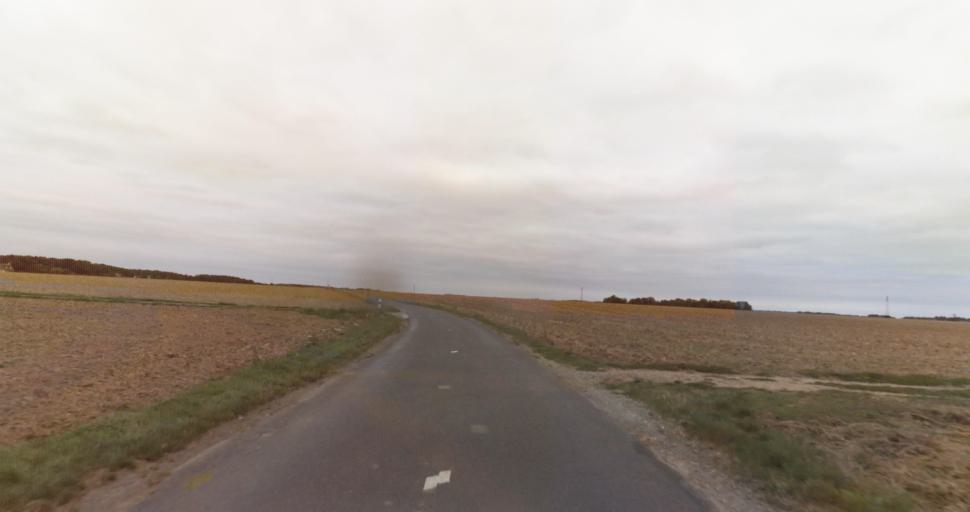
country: FR
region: Haute-Normandie
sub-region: Departement de l'Eure
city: Saint-Germain-sur-Avre
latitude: 48.7953
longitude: 1.2800
